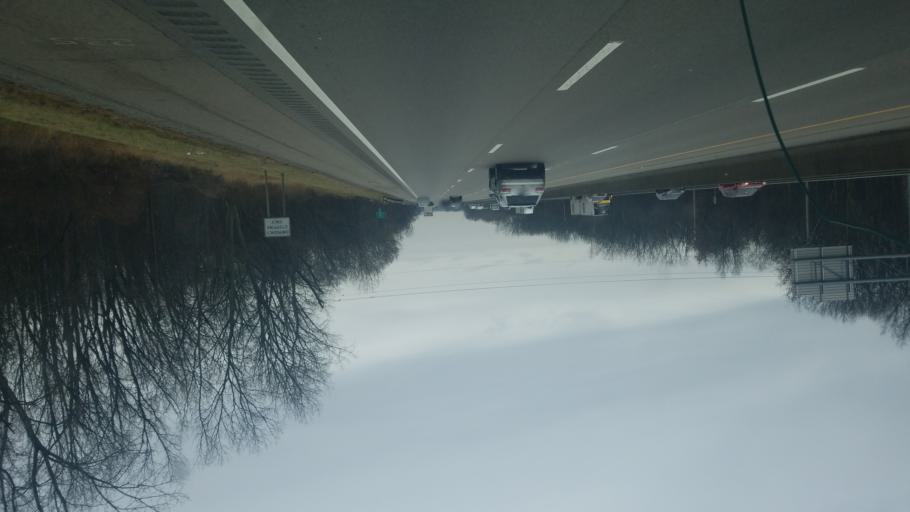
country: US
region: Ohio
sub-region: Clark County
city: Crystal Lakes
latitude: 39.8646
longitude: -84.0165
